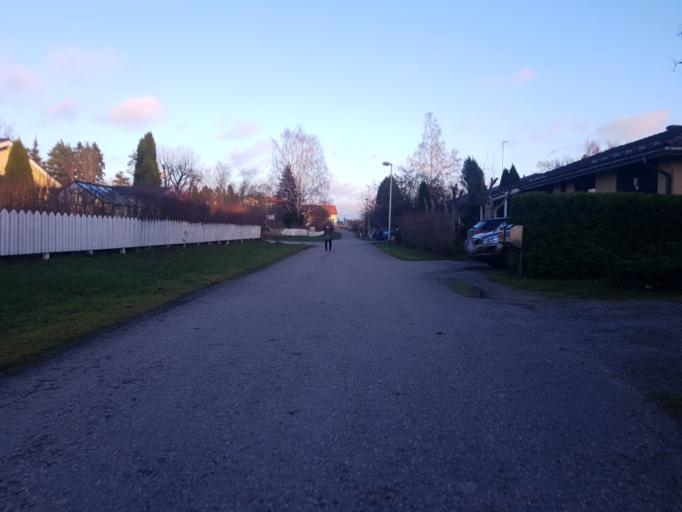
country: FI
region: Uusimaa
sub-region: Helsinki
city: Helsinki
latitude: 60.2751
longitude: 24.9153
